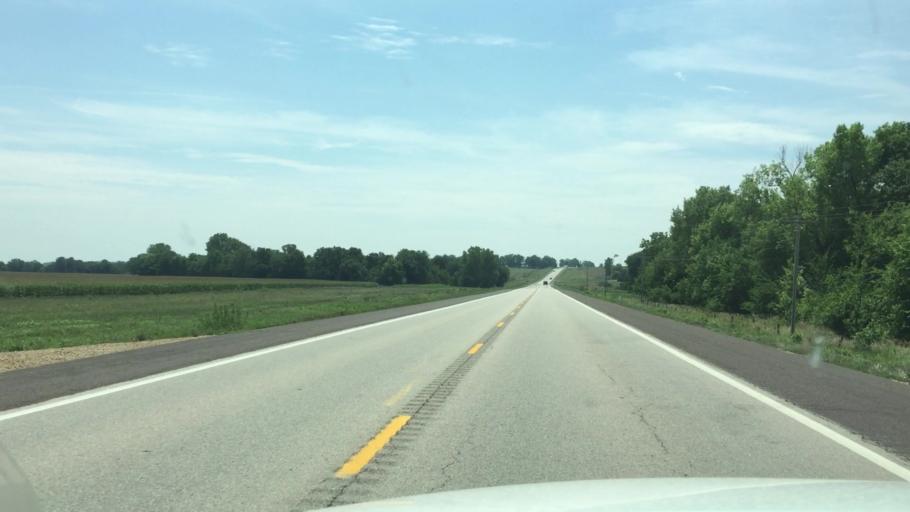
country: US
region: Kansas
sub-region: Jackson County
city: Holton
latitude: 39.5804
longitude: -95.7323
